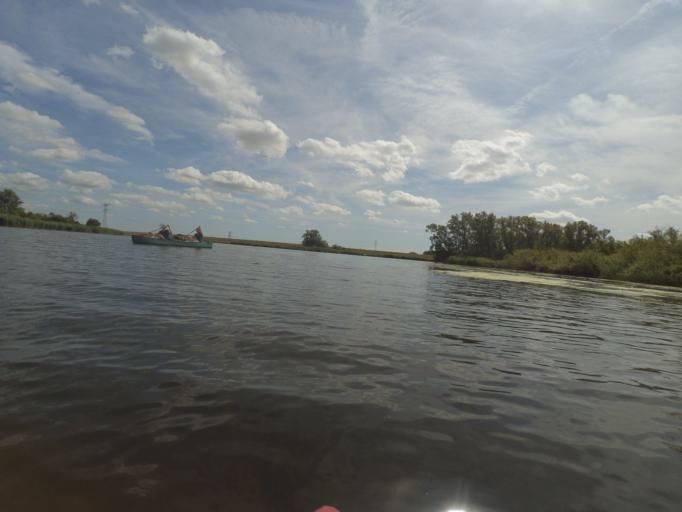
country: NL
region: North Brabant
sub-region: Gemeente Geertruidenberg
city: Geertruidenberg
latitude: 51.7564
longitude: 4.8497
